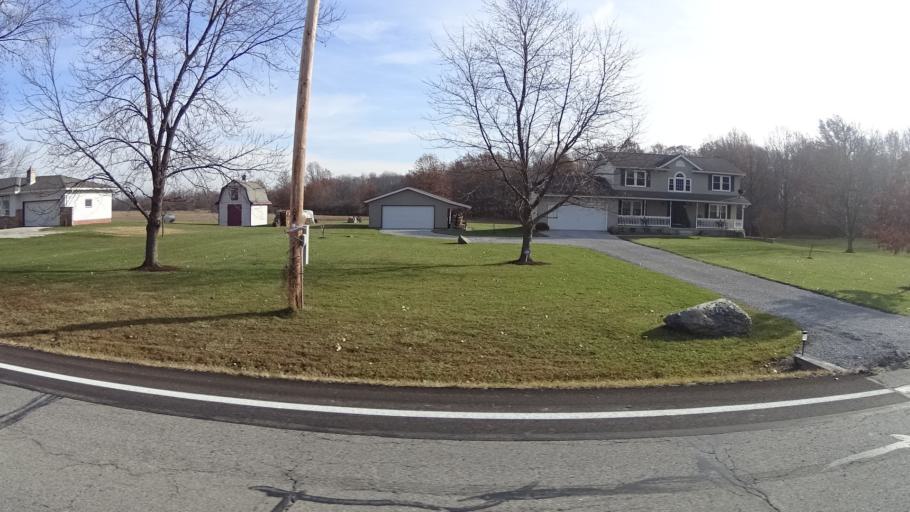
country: US
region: Ohio
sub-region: Lorain County
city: Eaton Estates
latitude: 41.2306
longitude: -81.9834
